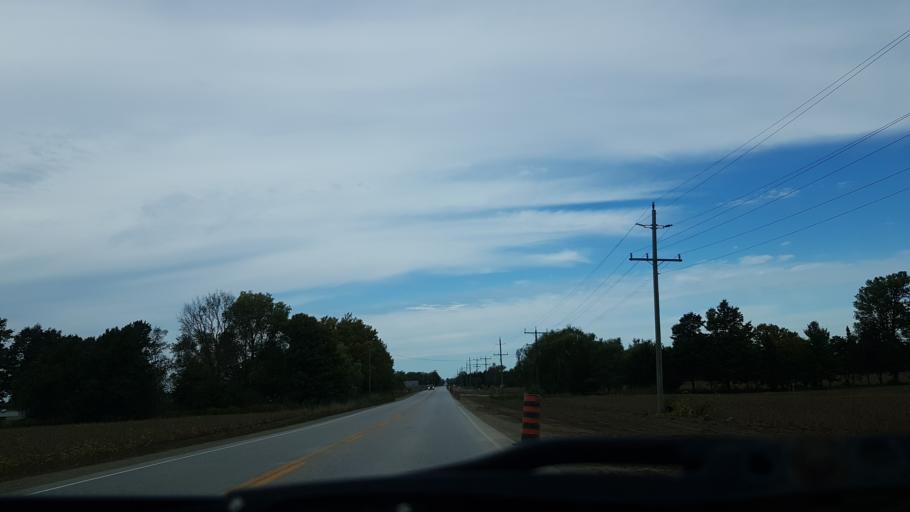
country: CA
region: Ontario
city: Wasaga Beach
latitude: 44.3830
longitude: -80.0883
